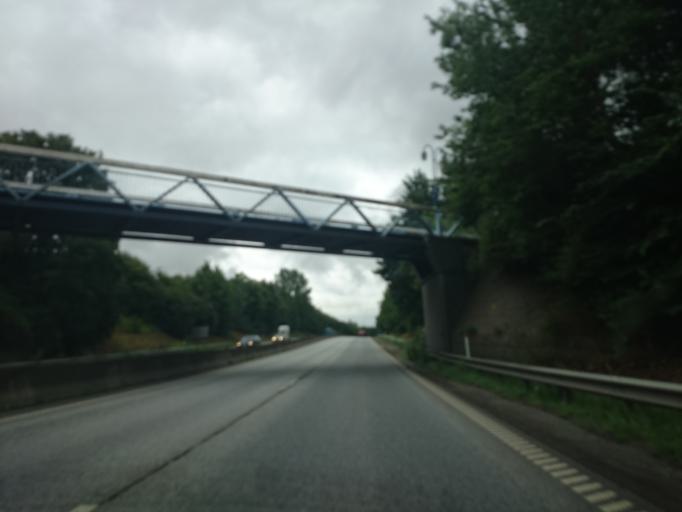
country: SE
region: Skane
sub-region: Lunds Kommun
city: Lund
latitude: 55.7036
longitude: 13.2196
